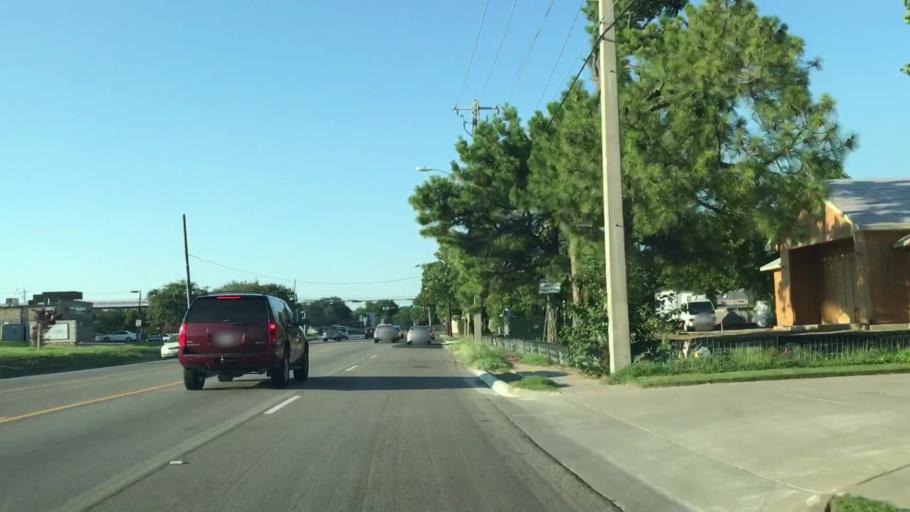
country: US
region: Texas
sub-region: Denton County
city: Denton
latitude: 33.2143
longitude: -97.1119
